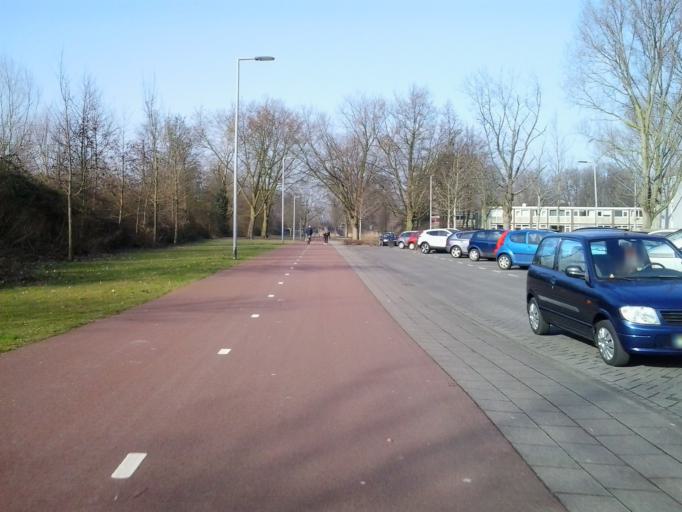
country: NL
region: South Holland
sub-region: Gemeente Rotterdam
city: Rotterdam
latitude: 51.9493
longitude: 4.4646
